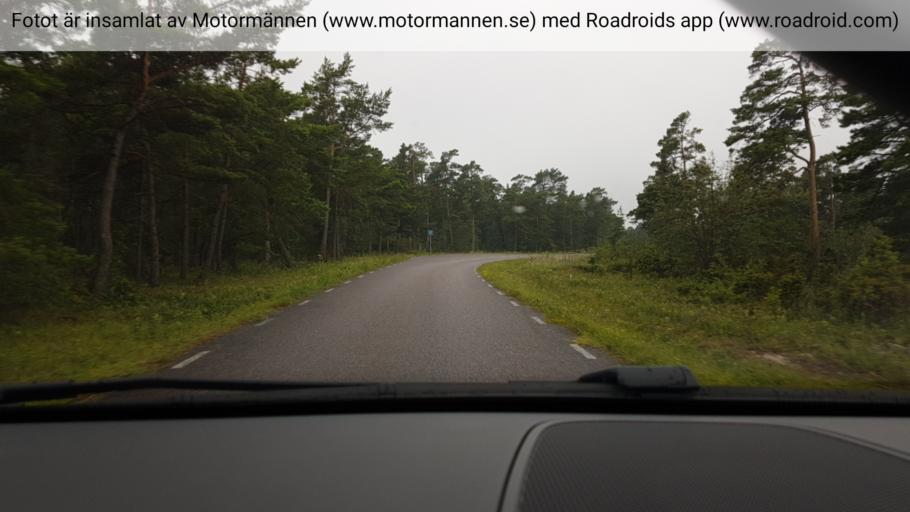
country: SE
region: Gotland
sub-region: Gotland
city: Slite
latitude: 57.8913
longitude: 18.7324
